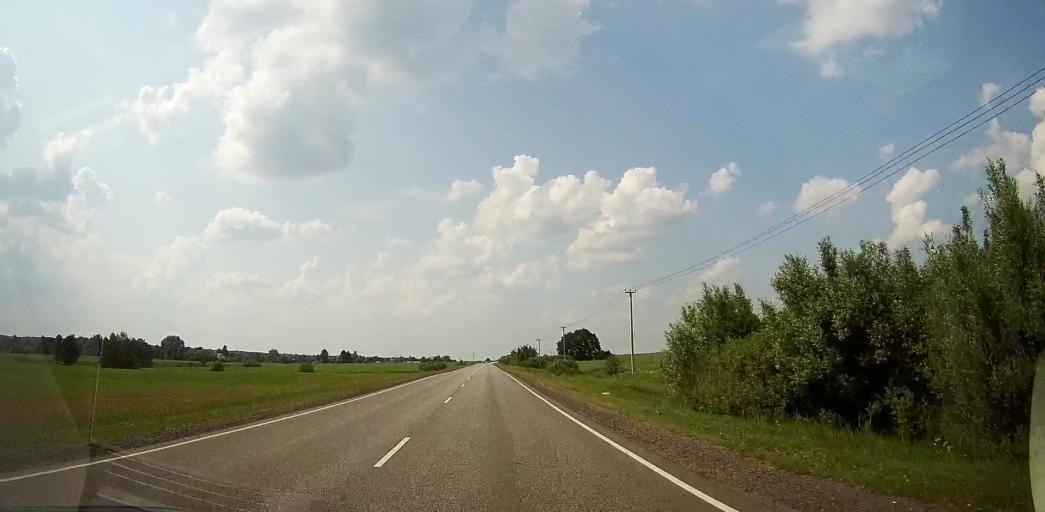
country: RU
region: Moskovskaya
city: Malino
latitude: 55.0299
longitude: 38.1654
